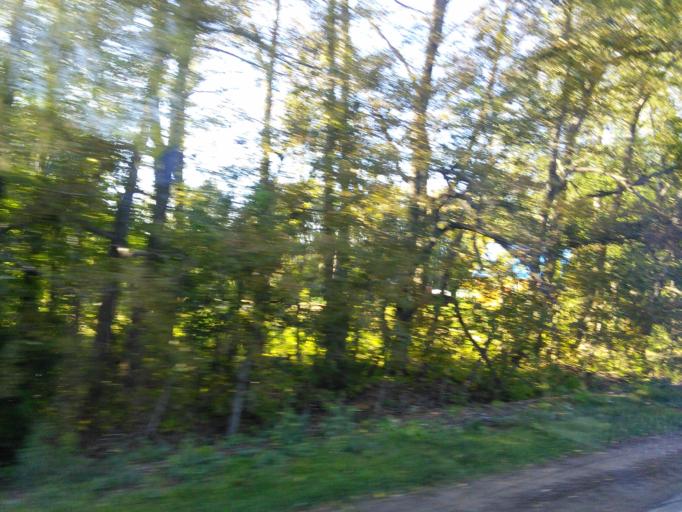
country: RU
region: Jaroslavl
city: Rybinsk
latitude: 58.2804
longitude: 38.8615
